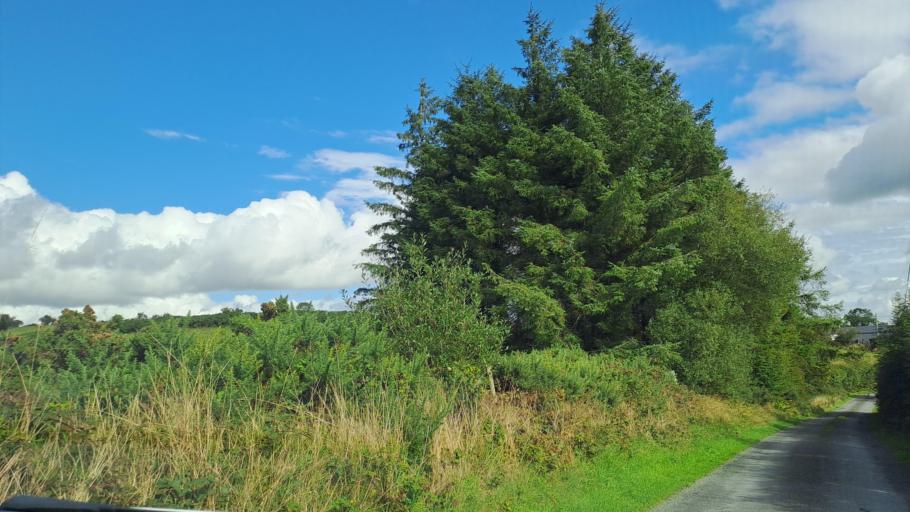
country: IE
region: Ulster
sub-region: An Cabhan
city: Kingscourt
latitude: 53.9488
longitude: -6.8596
